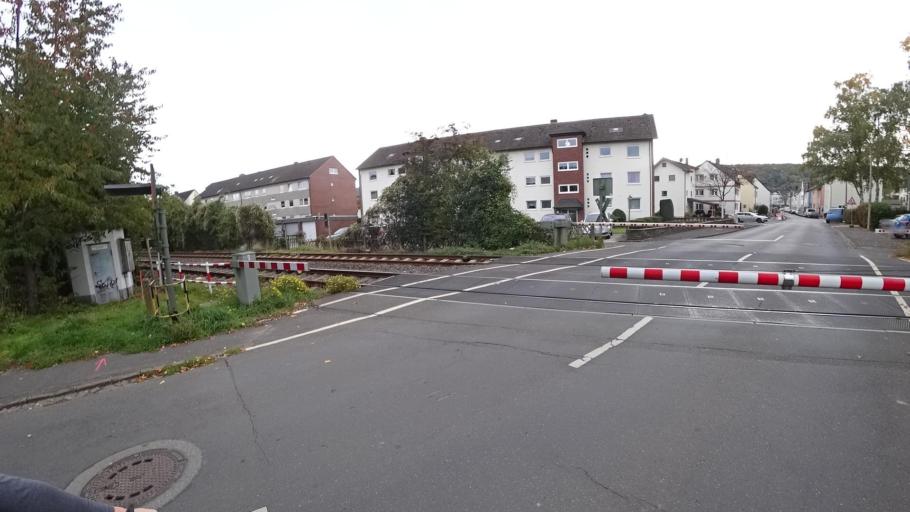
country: DE
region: Rheinland-Pfalz
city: Bad Neuenahr-Ahrweiler
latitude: 50.5476
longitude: 7.1266
